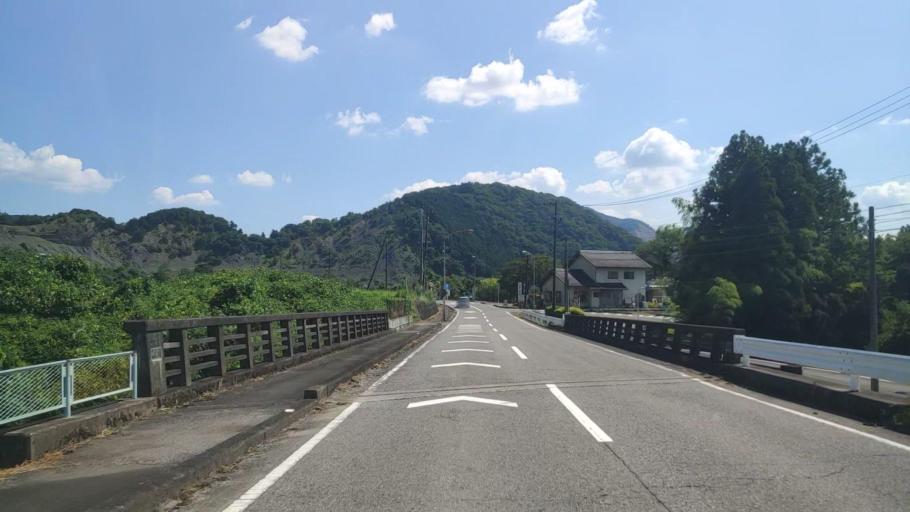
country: JP
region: Gifu
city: Godo
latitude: 35.5319
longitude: 136.6507
